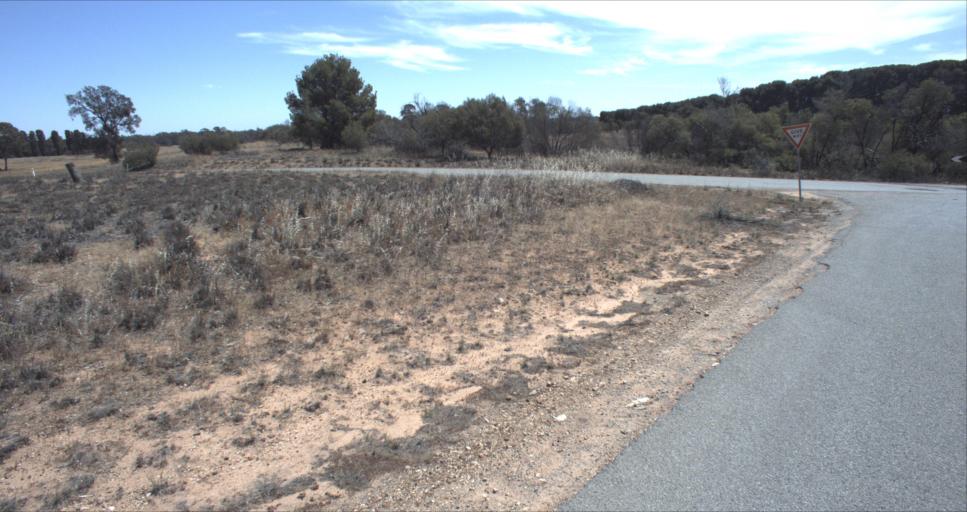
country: AU
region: New South Wales
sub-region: Leeton
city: Leeton
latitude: -34.6709
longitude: 146.4438
